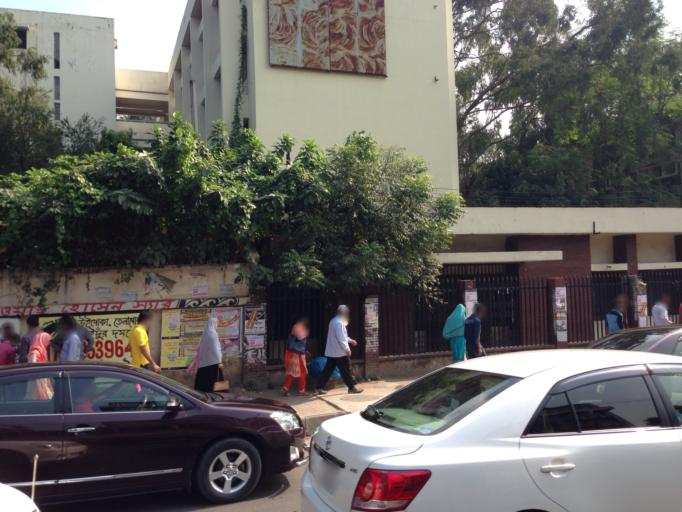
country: BD
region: Dhaka
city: Azimpur
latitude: 23.7400
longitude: 90.3833
